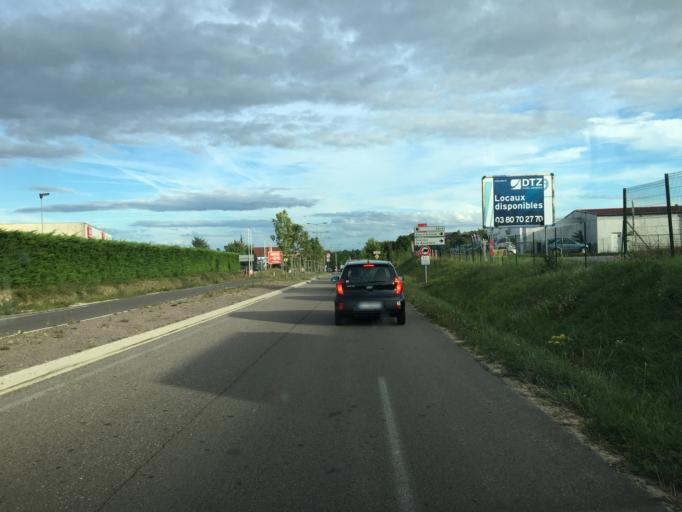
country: FR
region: Bourgogne
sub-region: Departement de la Cote-d'Or
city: Daix
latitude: 47.3443
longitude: 4.9982
